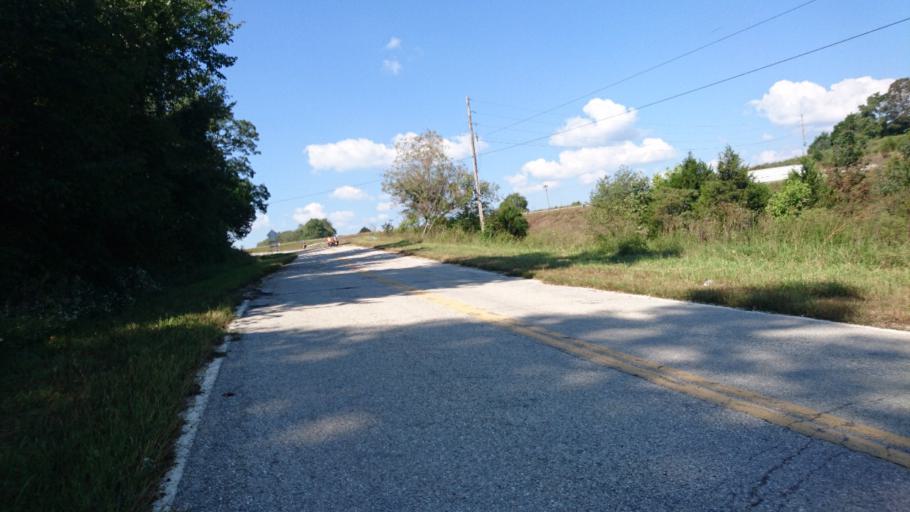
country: US
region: Missouri
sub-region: Pulaski County
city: Richland
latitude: 37.7578
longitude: -92.4555
